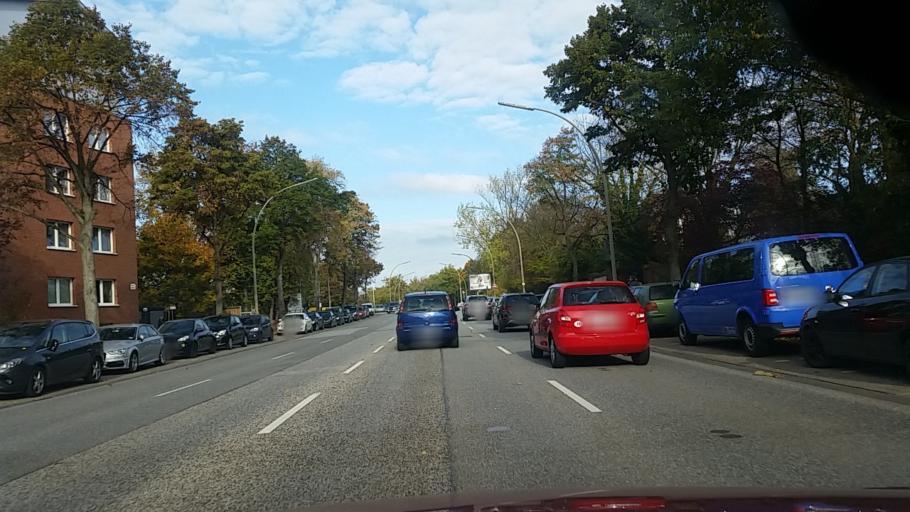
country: DE
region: Hamburg
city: Marienthal
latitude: 53.5608
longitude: 10.0803
